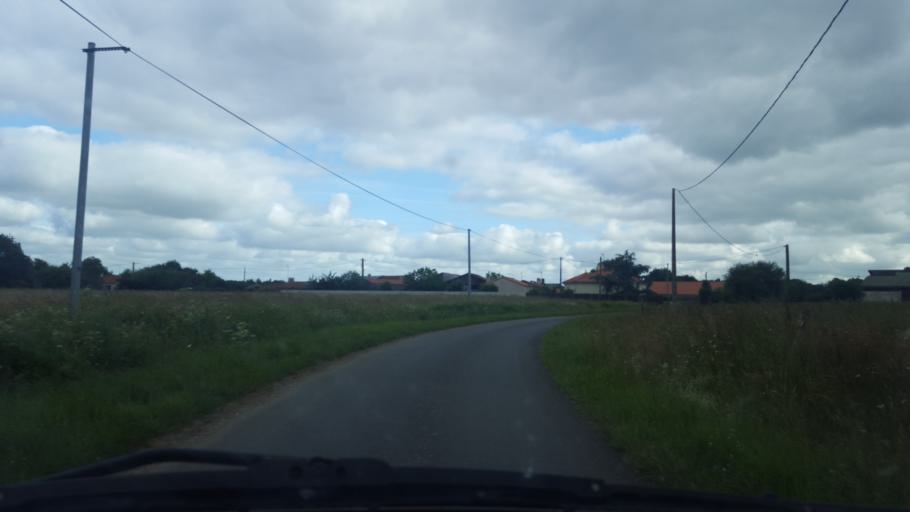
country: FR
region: Pays de la Loire
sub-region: Departement de la Loire-Atlantique
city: Saint-Philbert-de-Grand-Lieu
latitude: 47.0121
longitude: -1.6715
